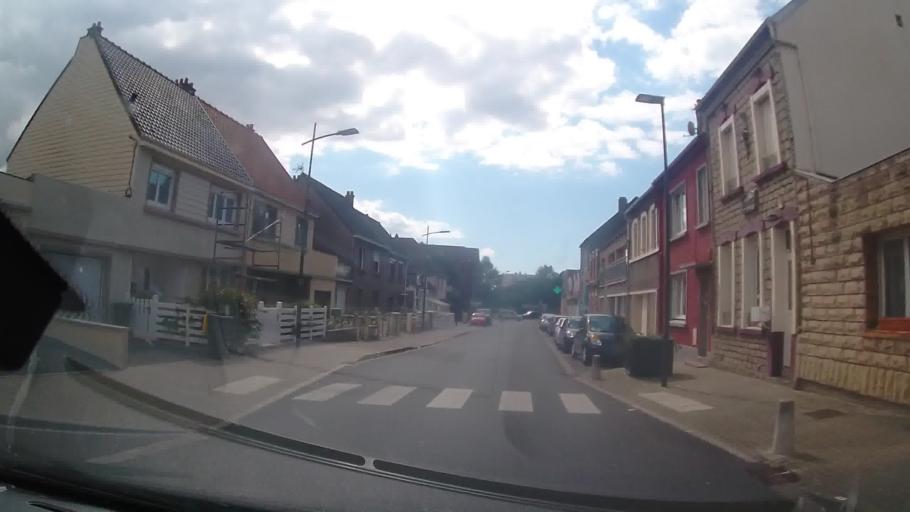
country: FR
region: Nord-Pas-de-Calais
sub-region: Departement du Pas-de-Calais
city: Saint-Martin-Boulogne
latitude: 50.7396
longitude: 1.6184
